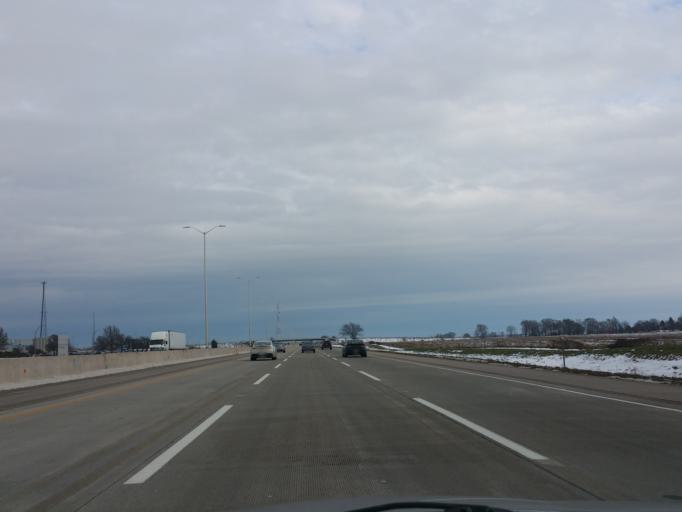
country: US
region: Illinois
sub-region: Boone County
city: Belvidere
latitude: 42.2334
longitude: -88.8722
